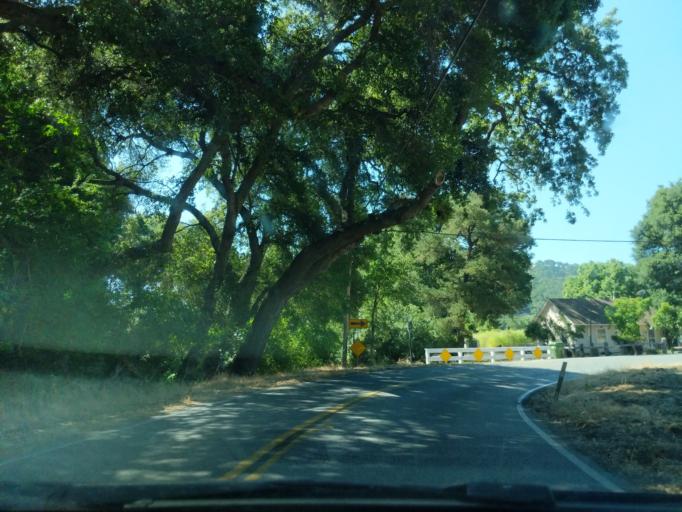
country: US
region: California
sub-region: Santa Clara County
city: Morgan Hill
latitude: 37.0933
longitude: -121.6685
